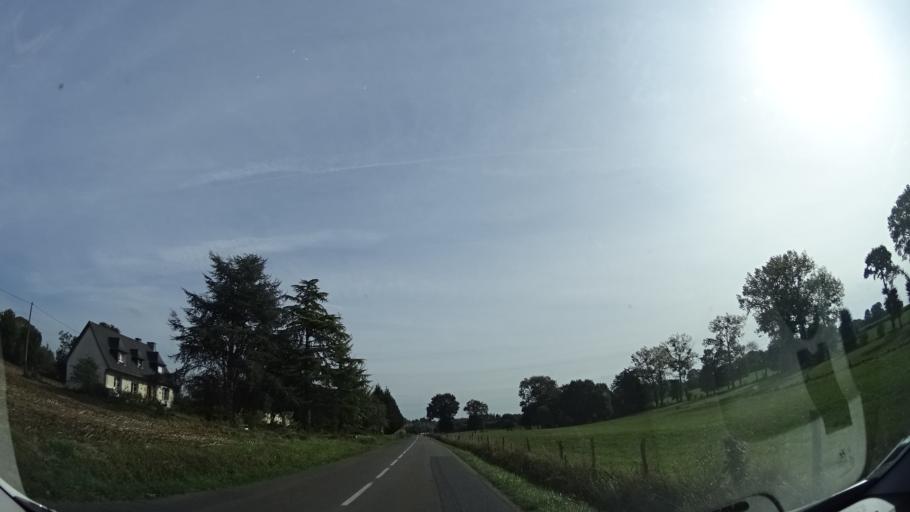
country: FR
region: Brittany
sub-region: Departement d'Ille-et-Vilaine
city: Melesse
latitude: 48.2166
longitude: -1.7244
